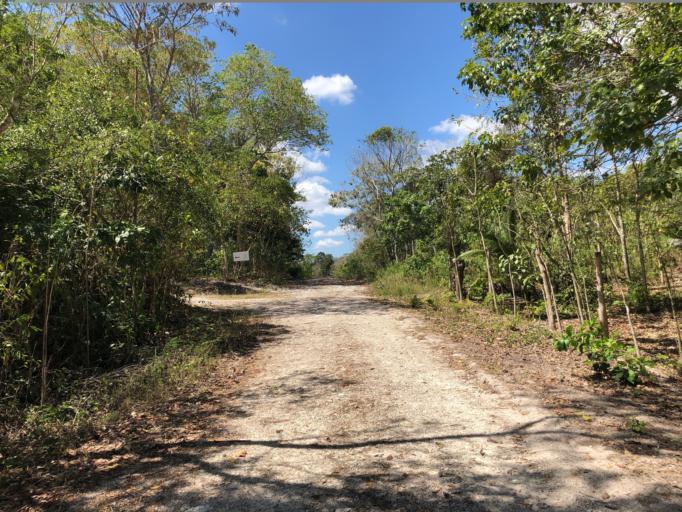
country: MX
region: Quintana Roo
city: Nicolas Bravo
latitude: 18.4496
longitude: -89.3081
